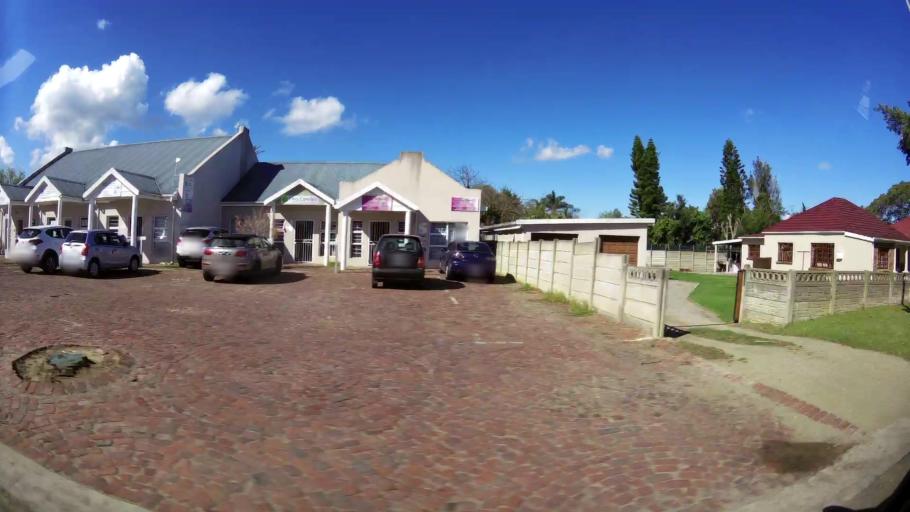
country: ZA
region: Western Cape
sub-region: Eden District Municipality
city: George
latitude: -33.9560
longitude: 22.4665
